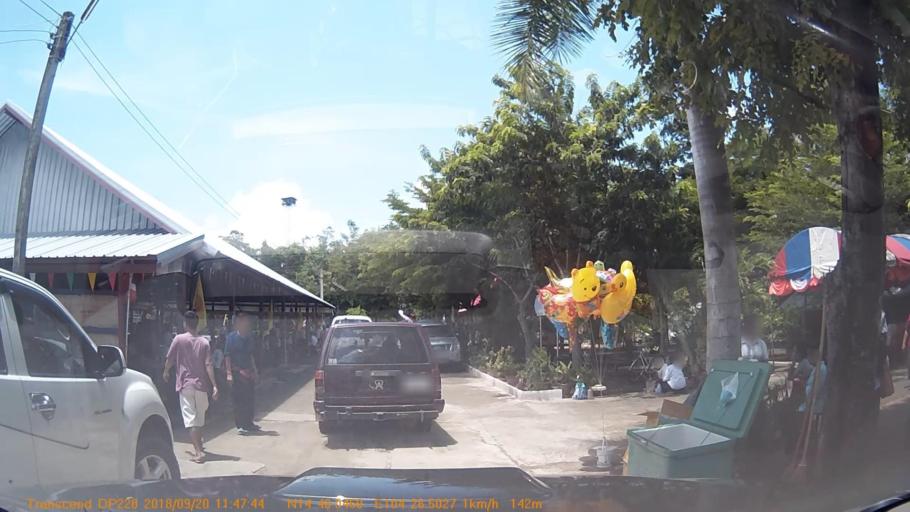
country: TH
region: Sisaket
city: Khun Han
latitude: 14.6674
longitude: 104.4417
